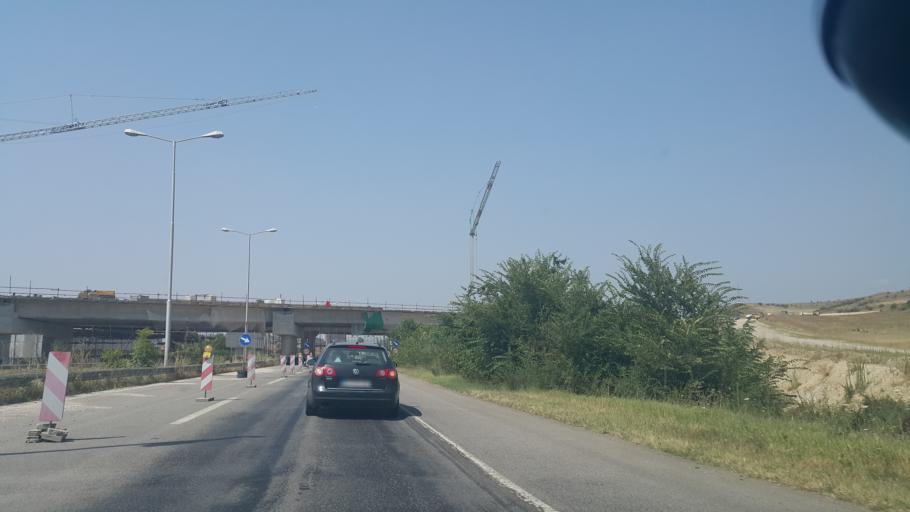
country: MK
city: Miladinovci
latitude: 41.9835
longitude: 21.6537
